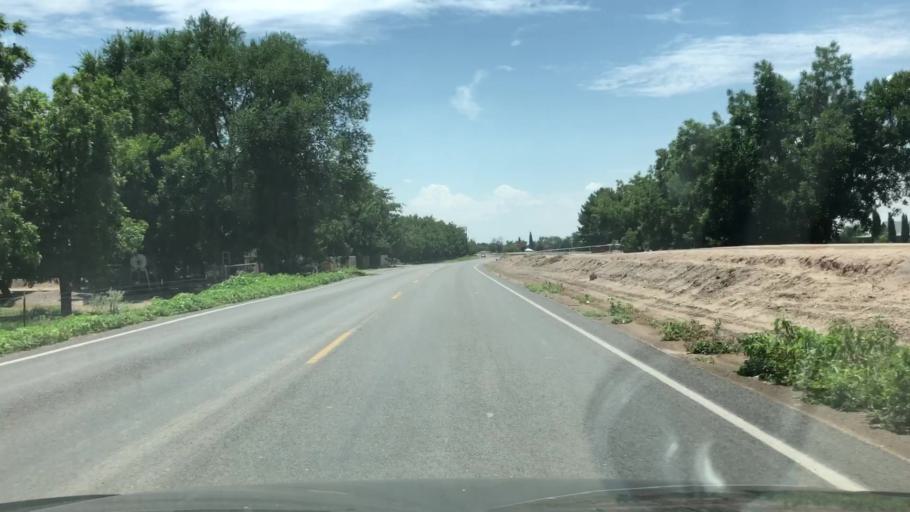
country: US
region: New Mexico
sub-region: Dona Ana County
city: Anthony
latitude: 32.0157
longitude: -106.6676
